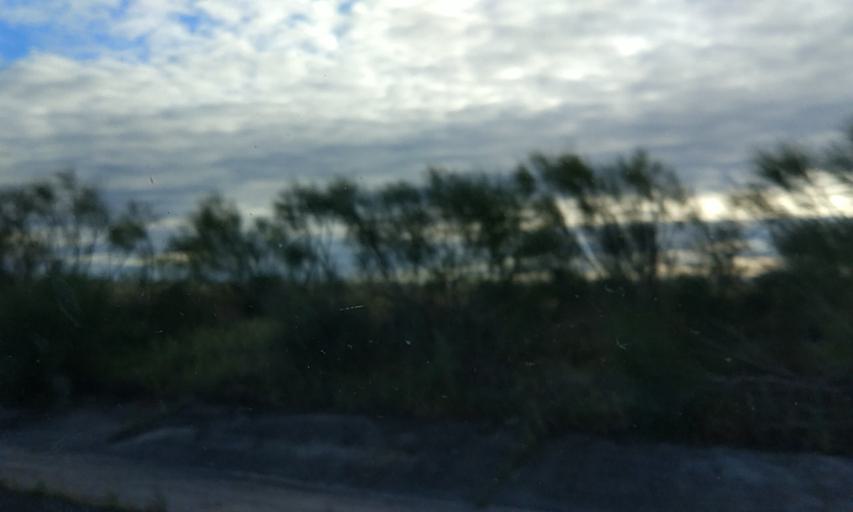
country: ES
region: Extremadura
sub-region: Provincia de Caceres
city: Santiago del Campo
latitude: 39.6613
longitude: -6.3926
